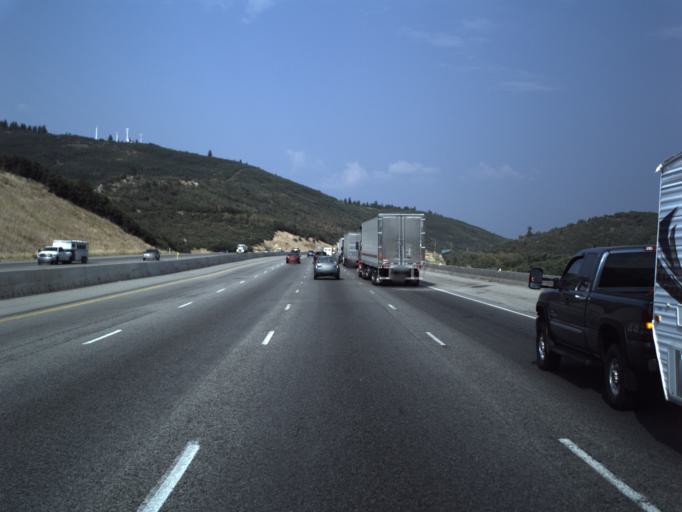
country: US
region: Utah
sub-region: Summit County
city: Summit Park
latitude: 40.7491
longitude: -111.6341
